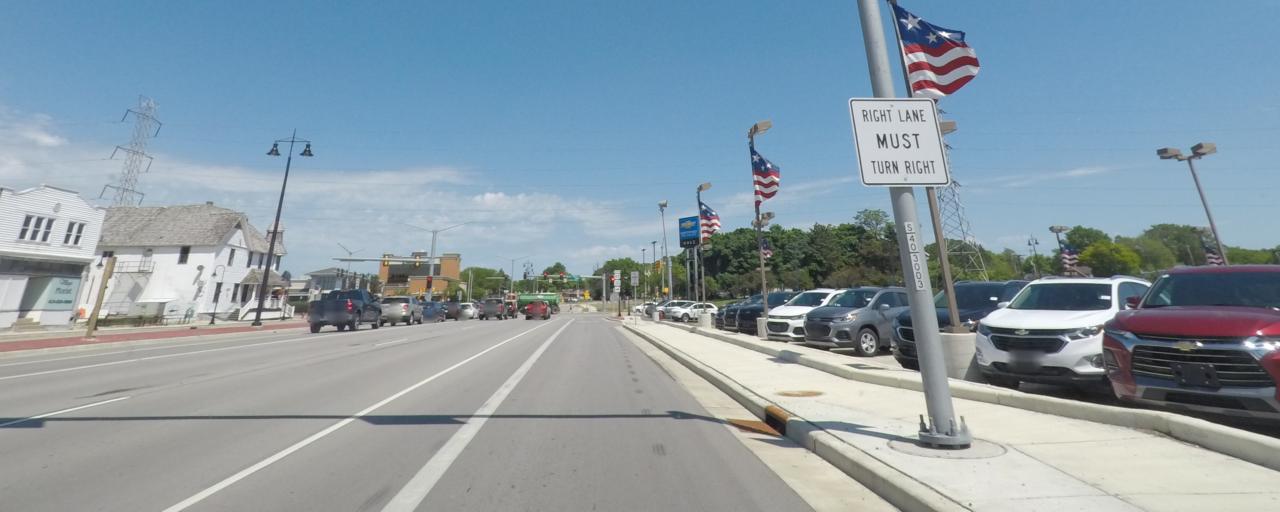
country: US
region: Wisconsin
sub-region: Milwaukee County
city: Hales Corners
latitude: 42.9372
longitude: -88.0498
